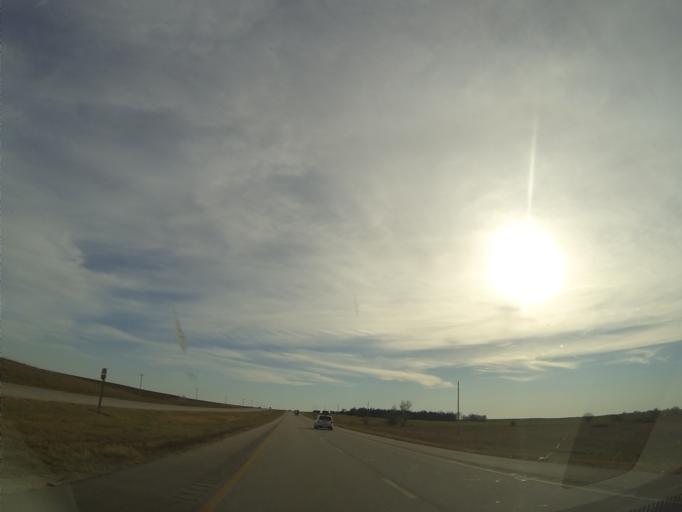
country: US
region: Kansas
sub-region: Ottawa County
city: Minneapolis
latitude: 39.1755
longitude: -97.6683
